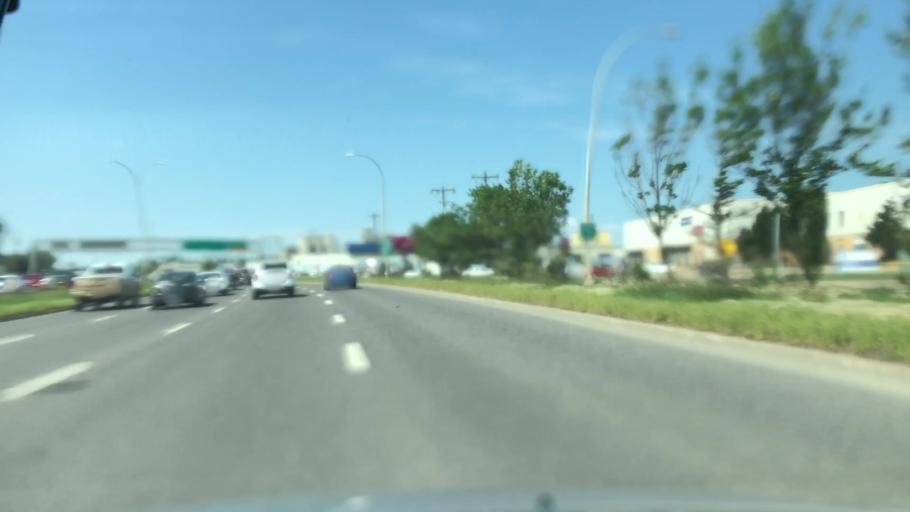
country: CA
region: Alberta
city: St. Albert
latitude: 53.5814
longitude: -113.5807
